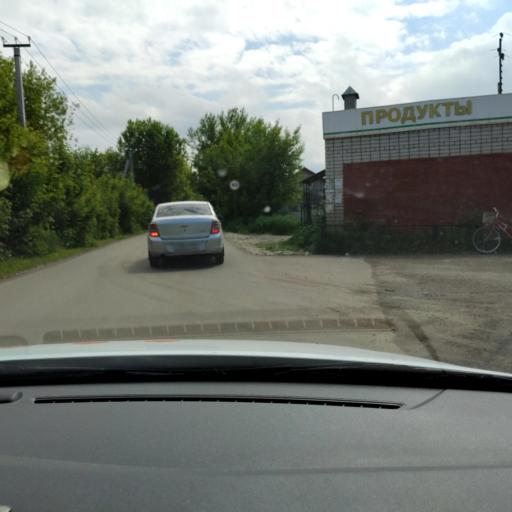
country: RU
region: Tatarstan
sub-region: Gorod Kazan'
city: Kazan
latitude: 55.7022
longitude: 49.0858
